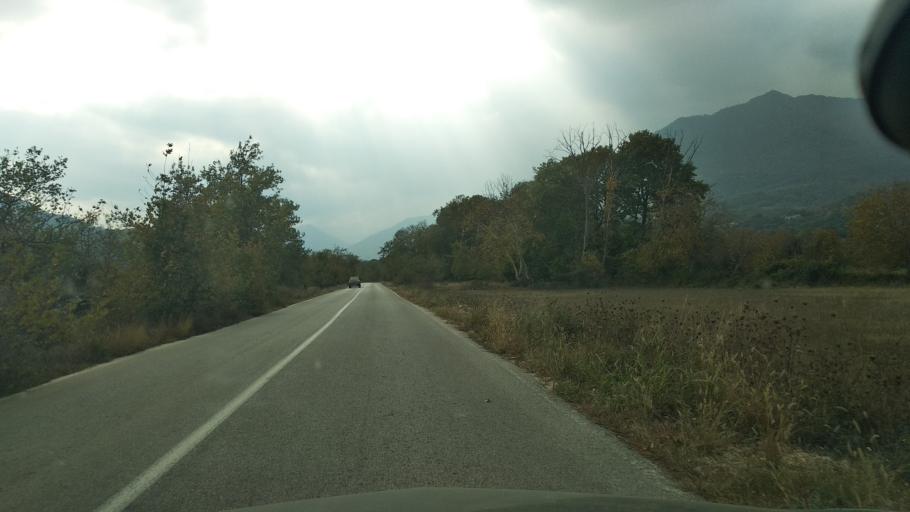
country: GR
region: Thessaly
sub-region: Trikala
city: Kastraki
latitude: 39.7005
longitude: 21.5254
